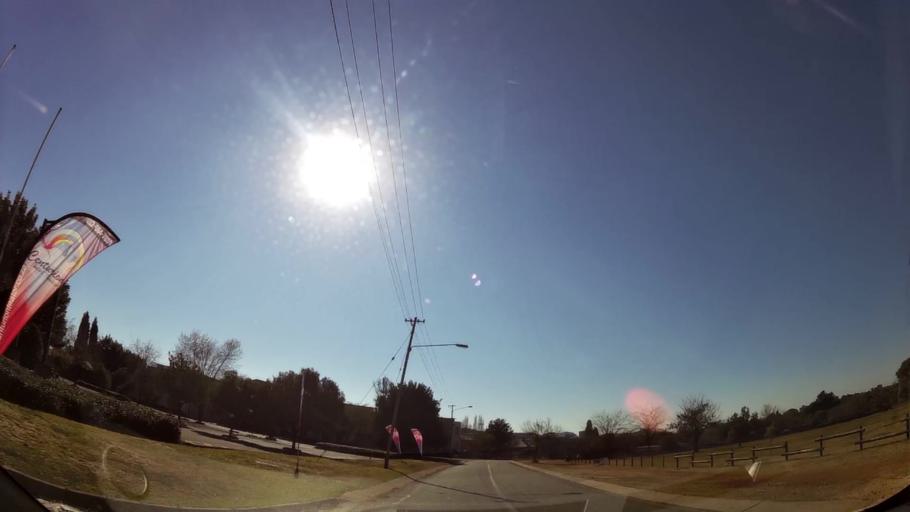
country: ZA
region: Gauteng
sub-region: City of Tshwane Metropolitan Municipality
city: Centurion
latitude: -25.8444
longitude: 28.2093
